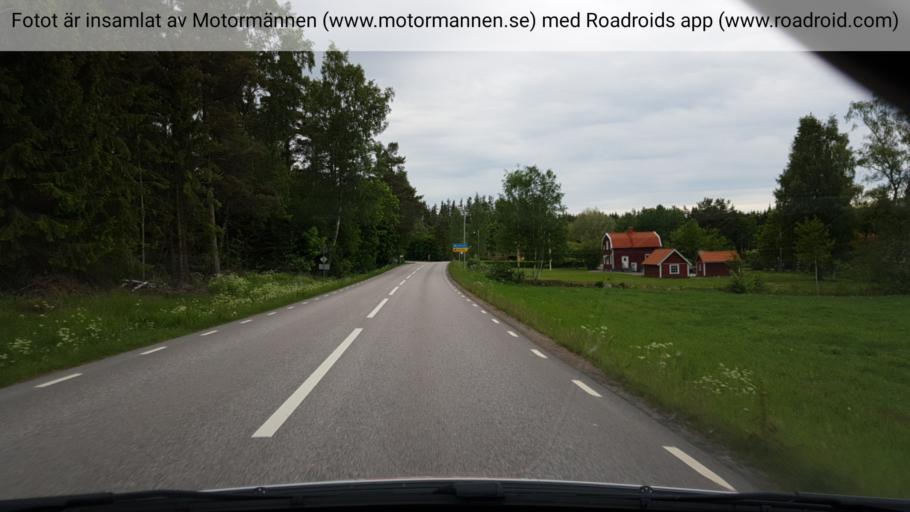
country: SE
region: OEstergoetland
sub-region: Motala Kommun
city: Borensberg
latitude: 58.6549
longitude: 15.3094
